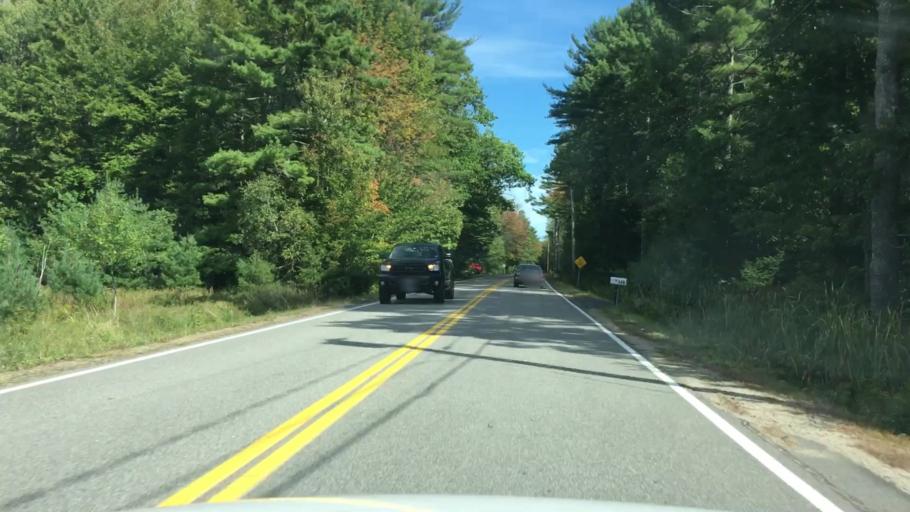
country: US
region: Maine
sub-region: Cumberland County
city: West Scarborough
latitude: 43.5870
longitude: -70.4438
